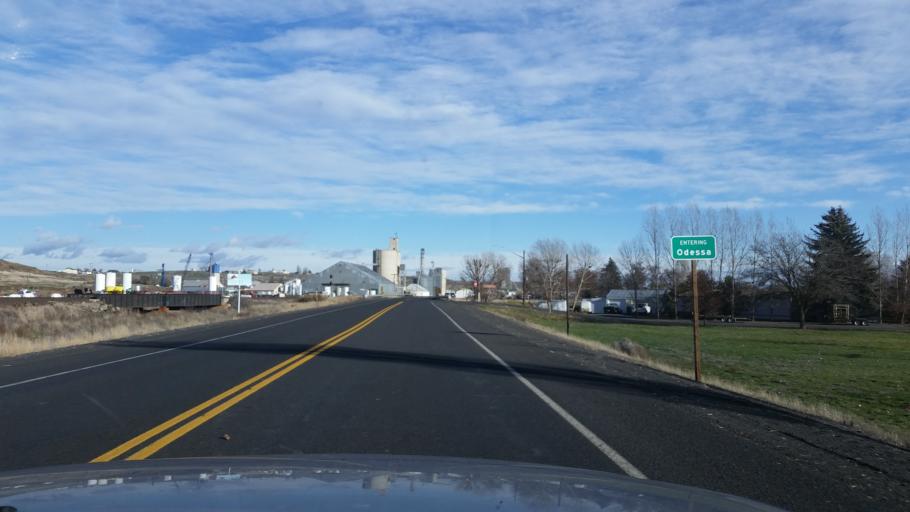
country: US
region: Washington
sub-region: Adams County
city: Ritzville
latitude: 47.3321
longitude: -118.7006
